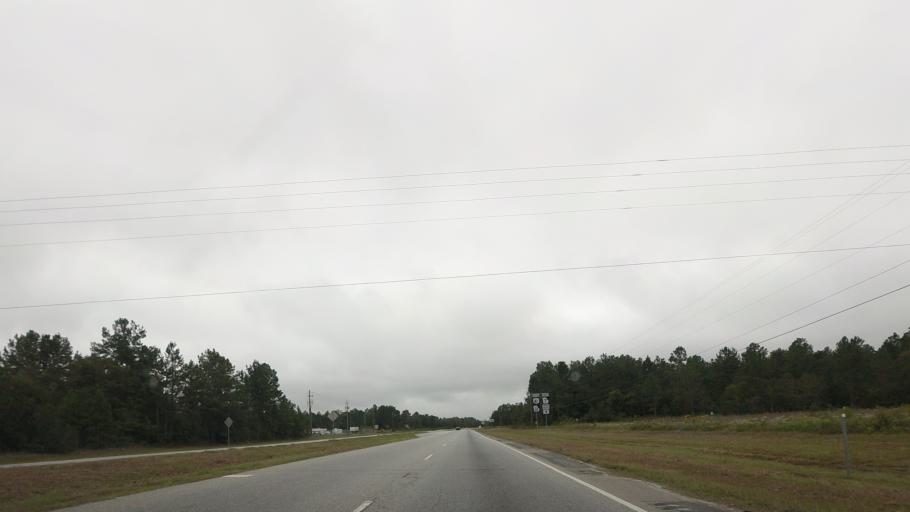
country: US
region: Georgia
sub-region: Lowndes County
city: Valdosta
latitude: 30.8478
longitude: -83.2289
